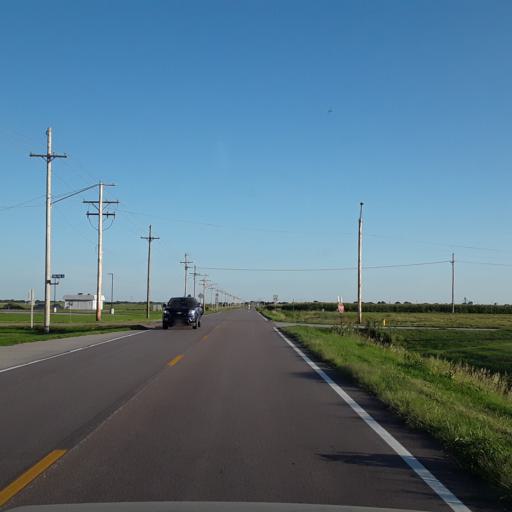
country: US
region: Nebraska
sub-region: Hall County
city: Grand Island
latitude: 40.9684
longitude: -98.3207
